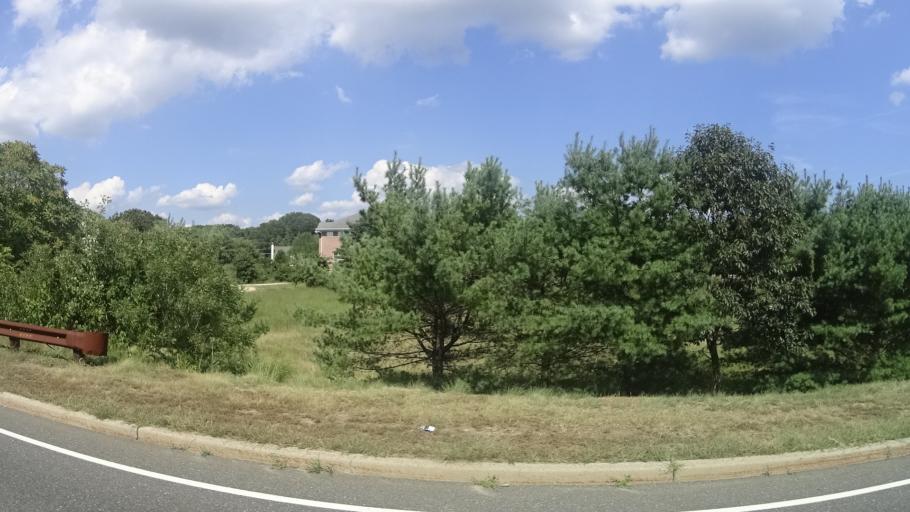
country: US
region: New Jersey
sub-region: Monmouth County
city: Ramtown
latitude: 40.1488
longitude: -74.1062
